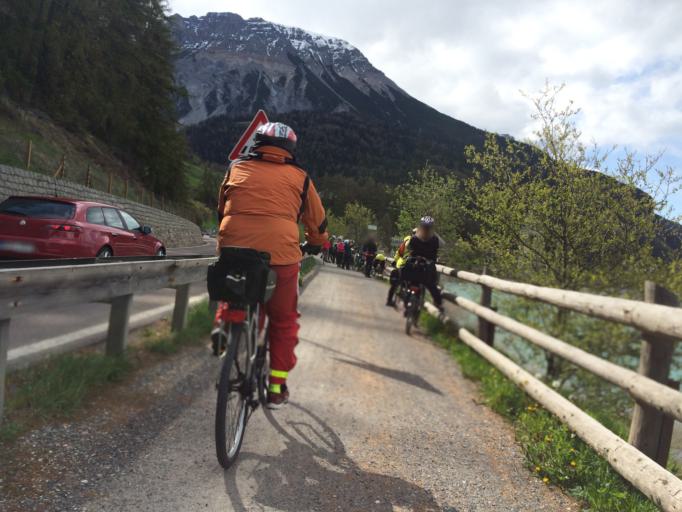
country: IT
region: Trentino-Alto Adige
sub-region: Bolzano
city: Curon Venosta
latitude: 46.8122
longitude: 10.5353
